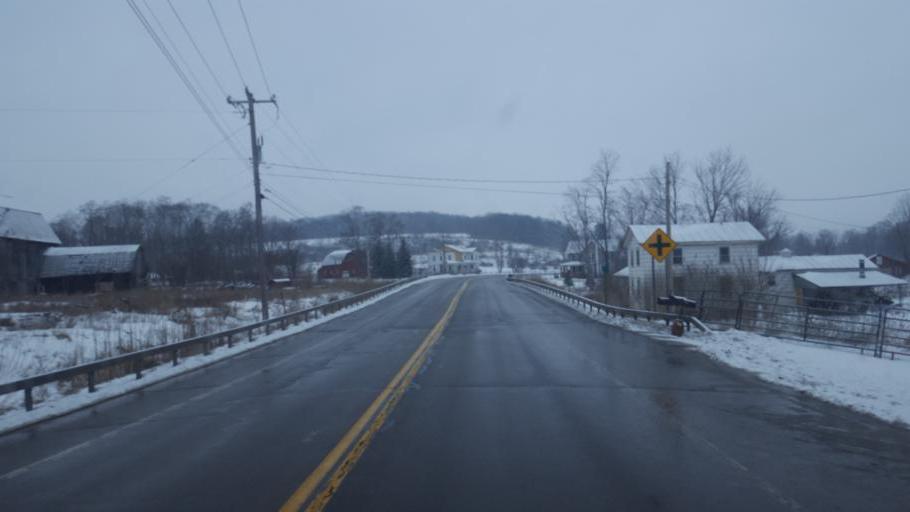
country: US
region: New York
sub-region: Steuben County
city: Canisteo
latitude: 42.1128
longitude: -77.4897
